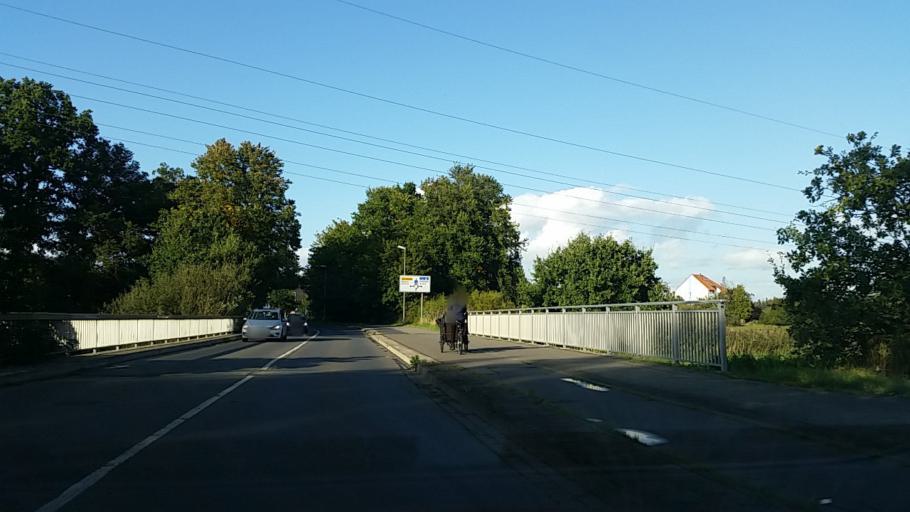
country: DE
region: Lower Saxony
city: Braunschweig
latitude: 52.2957
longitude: 10.5607
